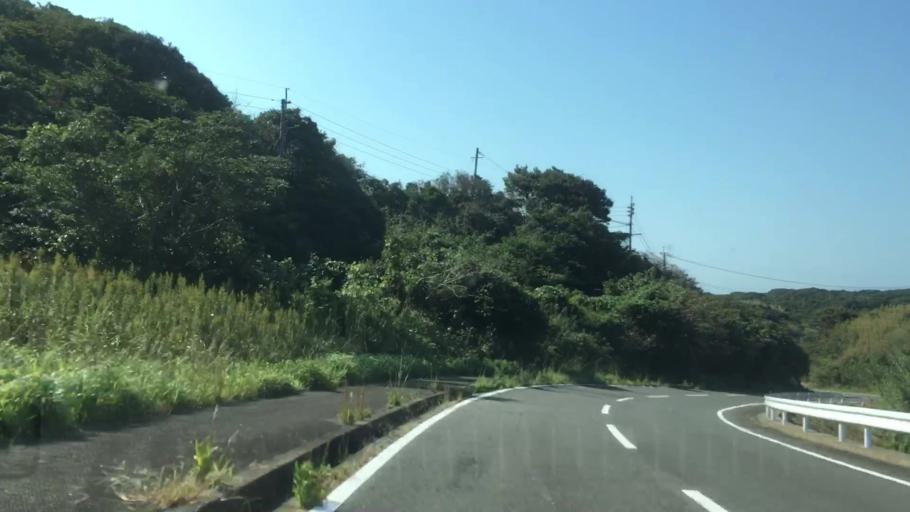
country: JP
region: Nagasaki
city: Sasebo
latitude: 33.0103
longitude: 129.5679
